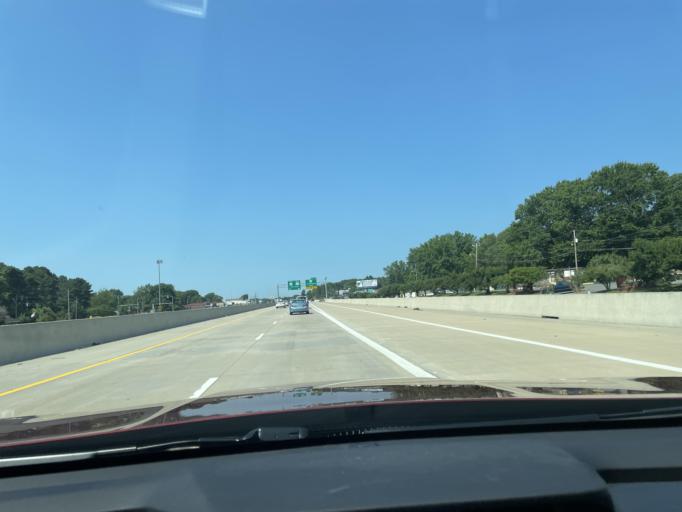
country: US
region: Arkansas
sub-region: Pulaski County
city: Jacksonville
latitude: 34.8943
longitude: -92.0967
